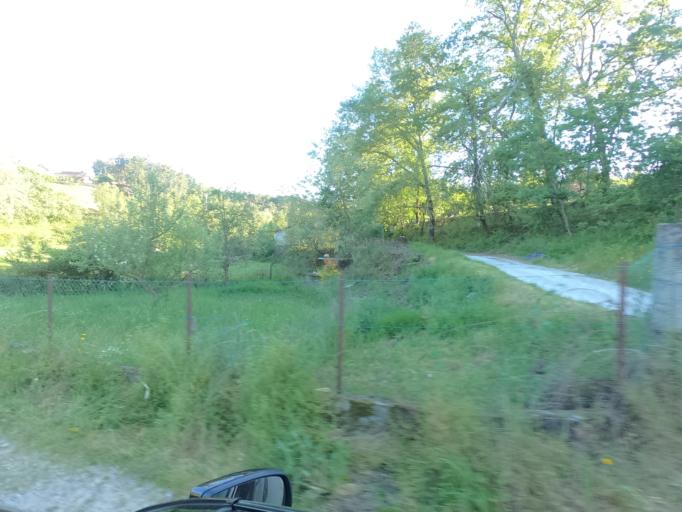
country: PT
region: Vila Real
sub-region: Vila Real
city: Vila Real
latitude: 41.3381
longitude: -7.7338
